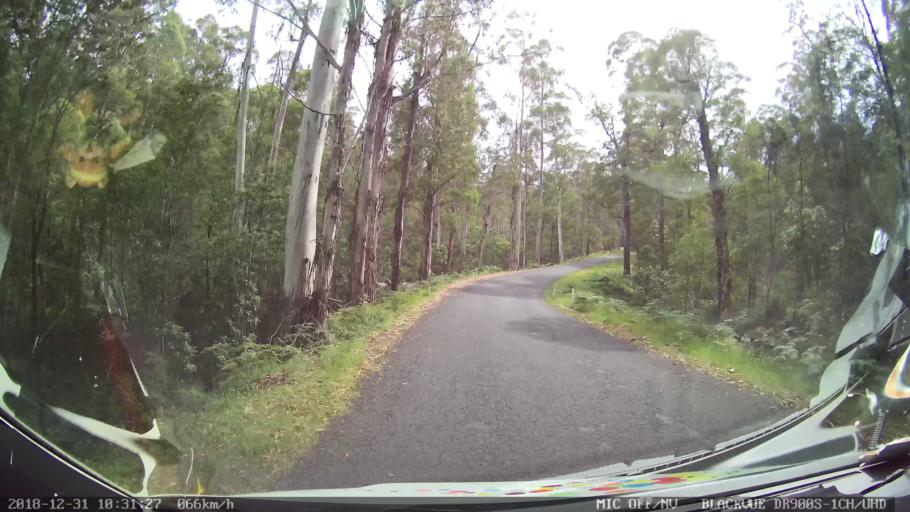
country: AU
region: New South Wales
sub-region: Snowy River
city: Jindabyne
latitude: -36.4575
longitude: 148.1581
